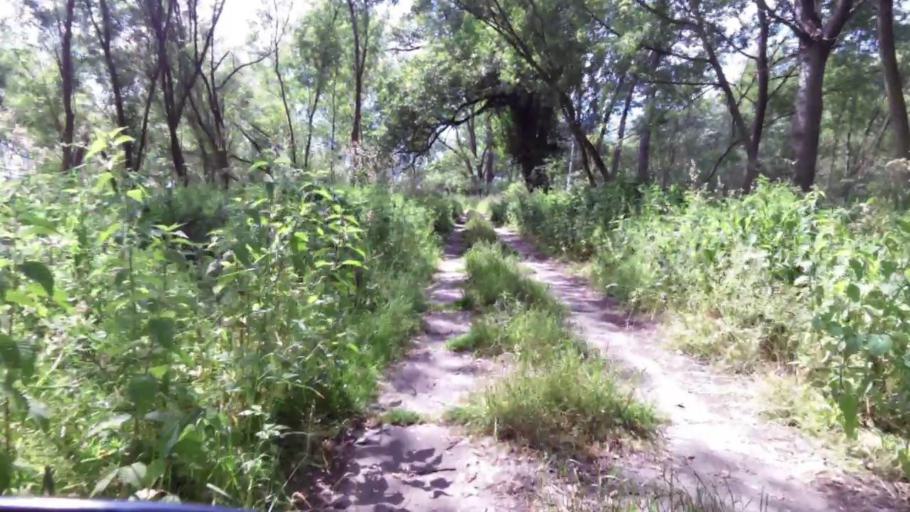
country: PL
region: West Pomeranian Voivodeship
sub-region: Powiat kamienski
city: Wolin
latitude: 53.8489
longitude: 14.5769
